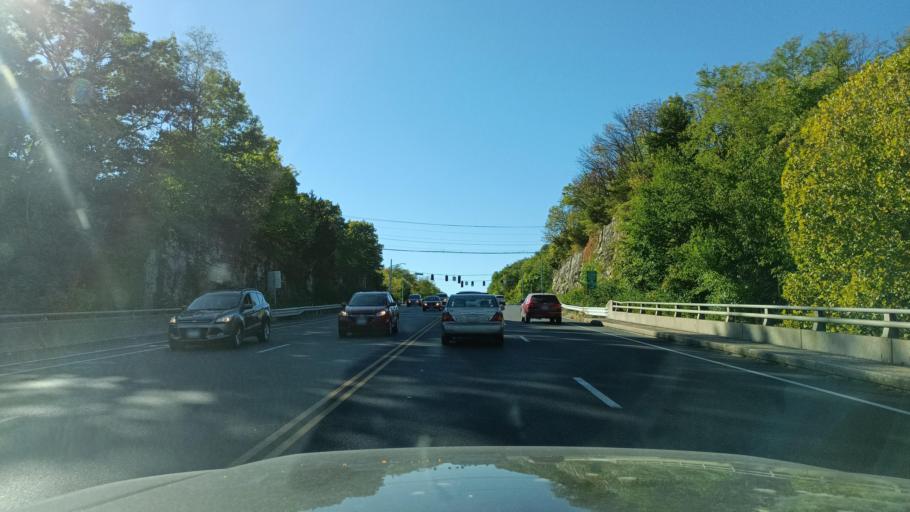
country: US
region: Missouri
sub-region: Boone County
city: Columbia
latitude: 38.9327
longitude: -92.3136
